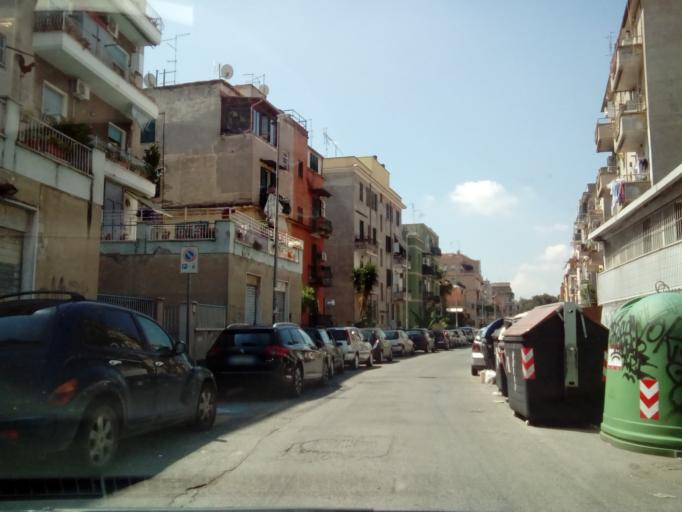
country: IT
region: Latium
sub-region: Citta metropolitana di Roma Capitale
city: Rome
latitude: 41.8776
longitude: 12.5711
